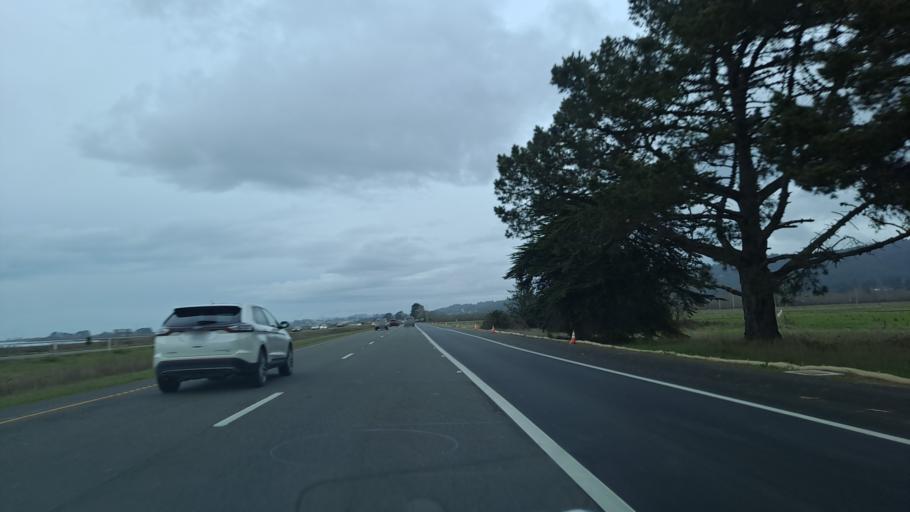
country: US
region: California
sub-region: Humboldt County
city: Bayside
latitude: 40.8355
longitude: -124.0816
